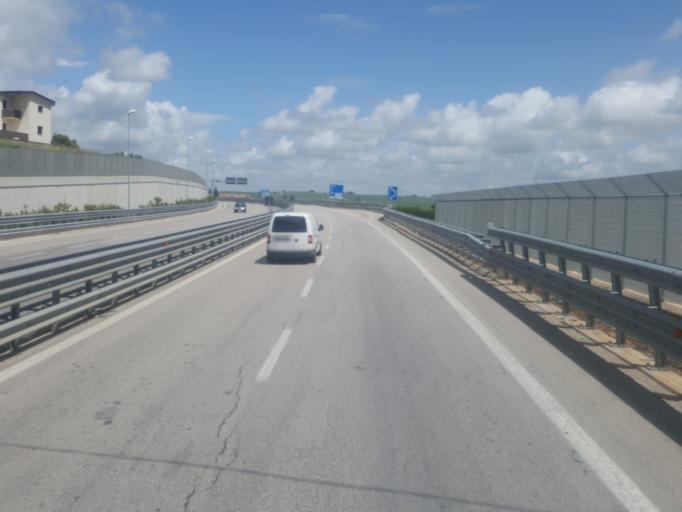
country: IT
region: Basilicate
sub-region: Provincia di Matera
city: Matera
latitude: 40.6910
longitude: 16.5910
